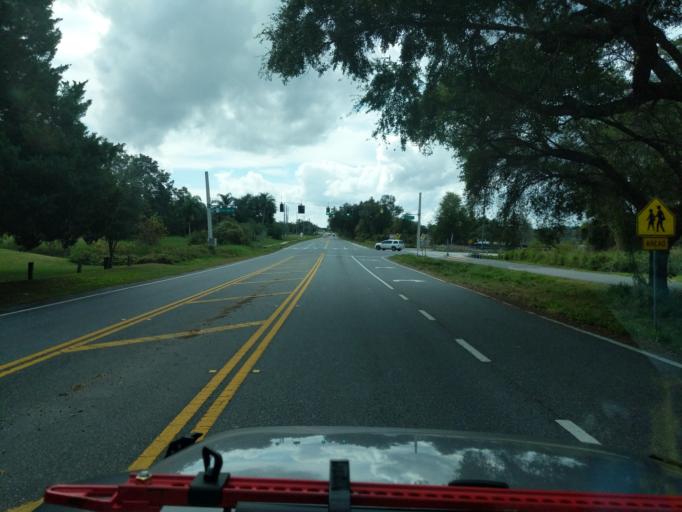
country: US
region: Florida
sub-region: Lake County
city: Groveland
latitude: 28.5656
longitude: -81.8177
